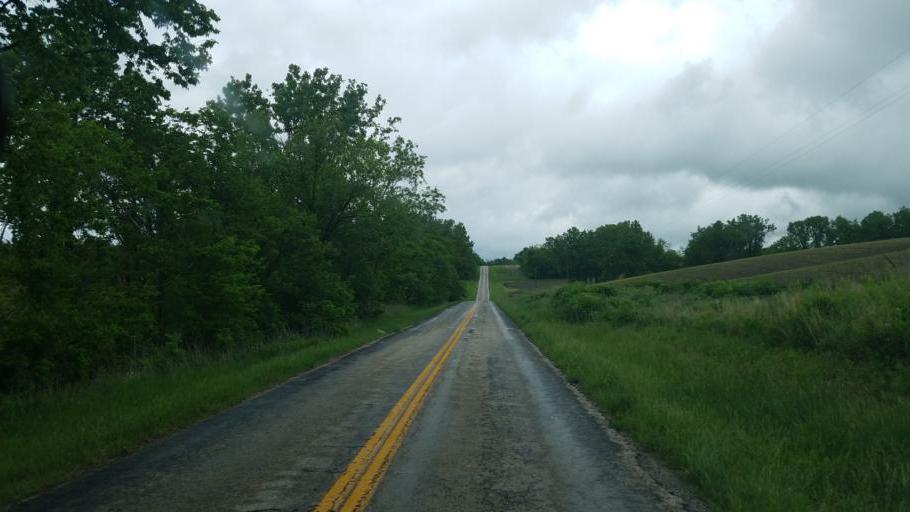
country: US
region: Missouri
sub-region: Mercer County
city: Princeton
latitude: 40.4943
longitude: -93.7225
